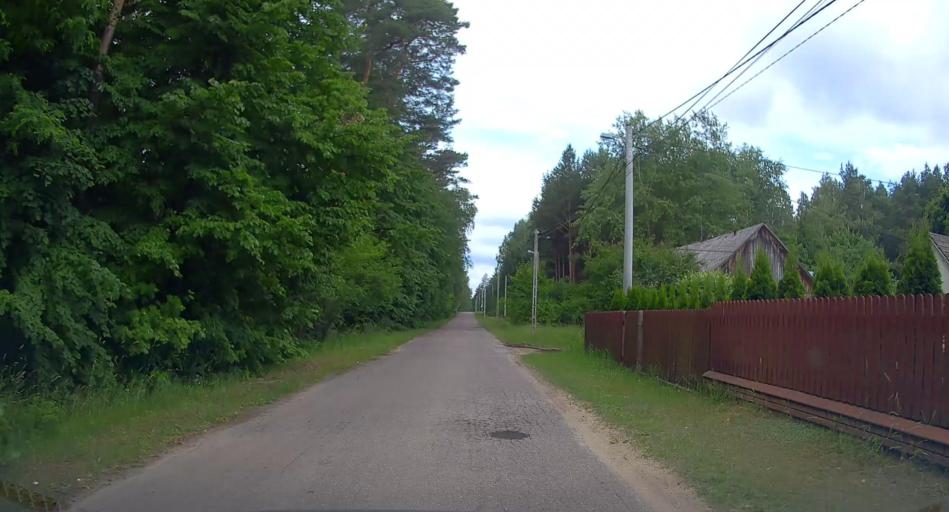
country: PL
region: Masovian Voivodeship
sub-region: Powiat ostrowski
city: Brok
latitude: 52.7422
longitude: 21.7431
